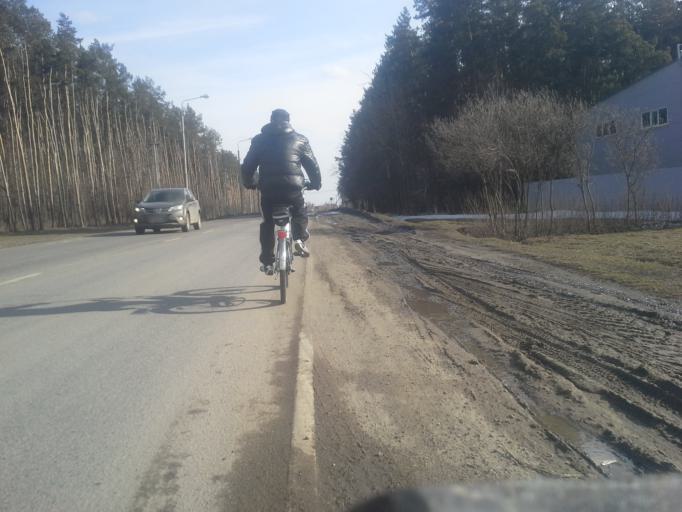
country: RU
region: Moskovskaya
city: Shcherbinka
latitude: 55.4846
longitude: 37.5187
